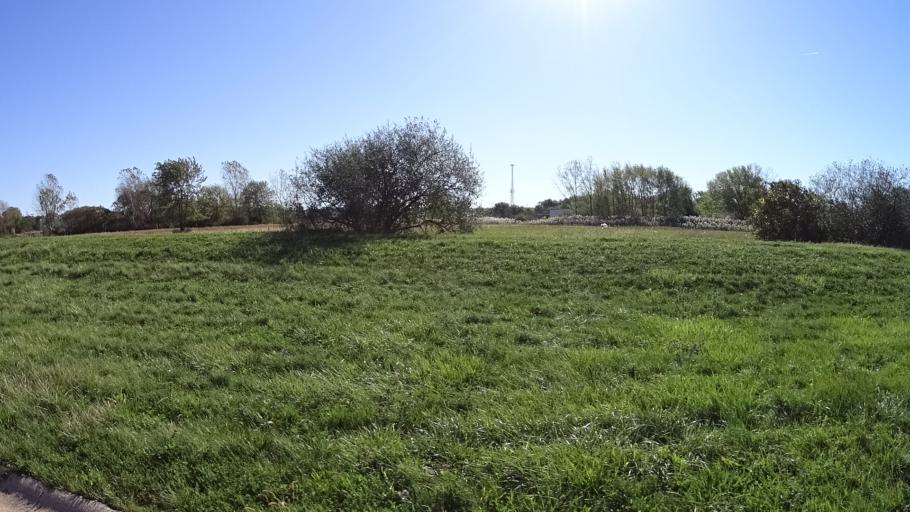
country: US
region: Ohio
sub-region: Lorain County
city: Amherst
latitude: 41.4204
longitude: -82.2153
